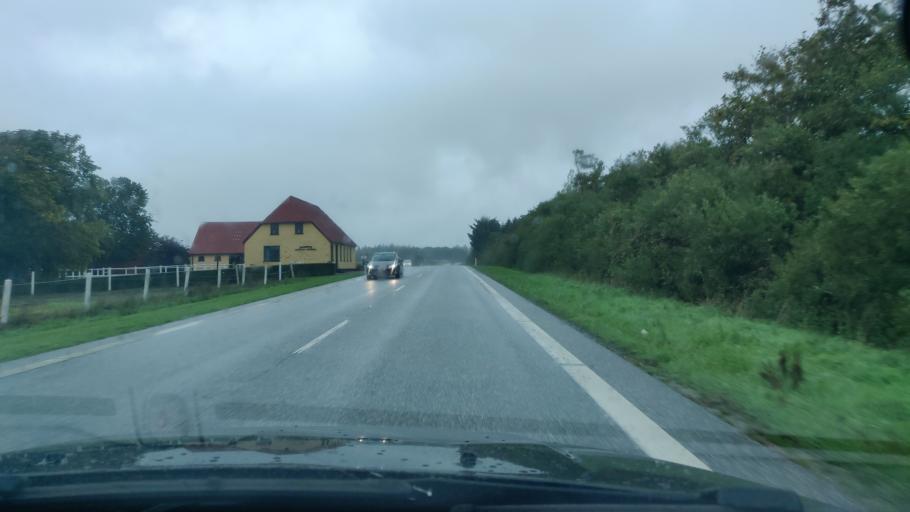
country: DK
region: North Denmark
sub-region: Thisted Kommune
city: Hurup
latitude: 56.8298
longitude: 8.5042
